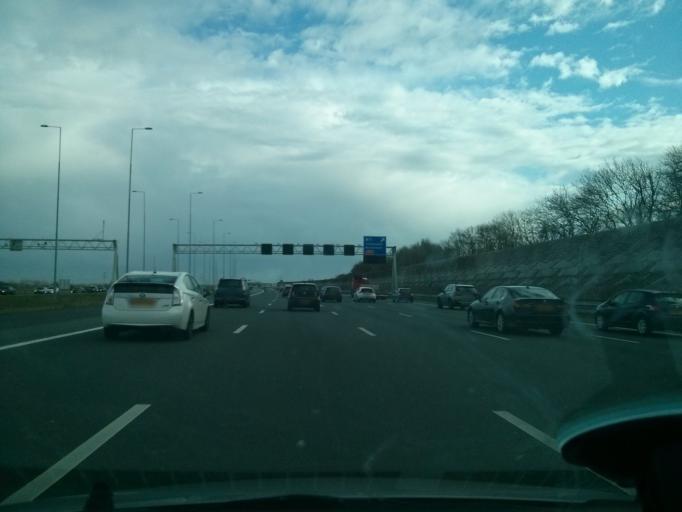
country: NL
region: Utrecht
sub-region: Stichtse Vecht
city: Vreeland
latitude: 52.2341
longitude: 4.9770
